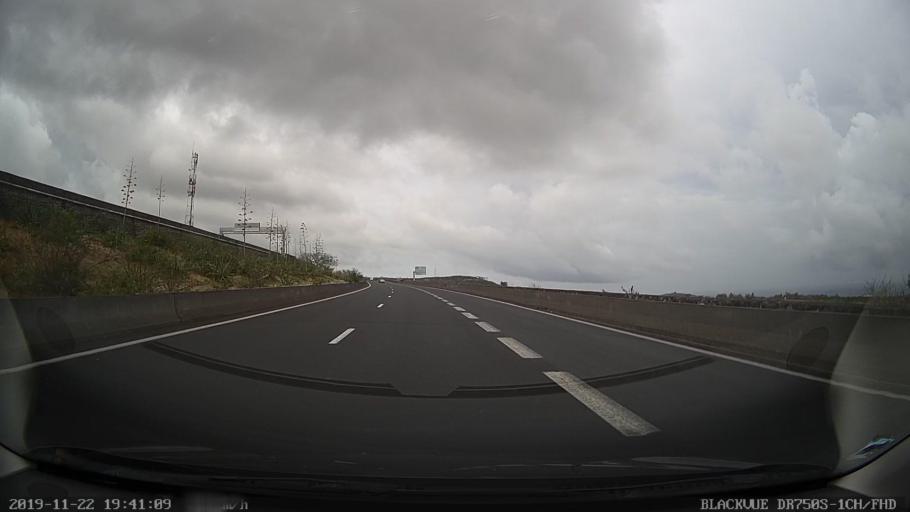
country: RE
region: Reunion
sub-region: Reunion
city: Saint-Paul
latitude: -21.0318
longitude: 55.2492
